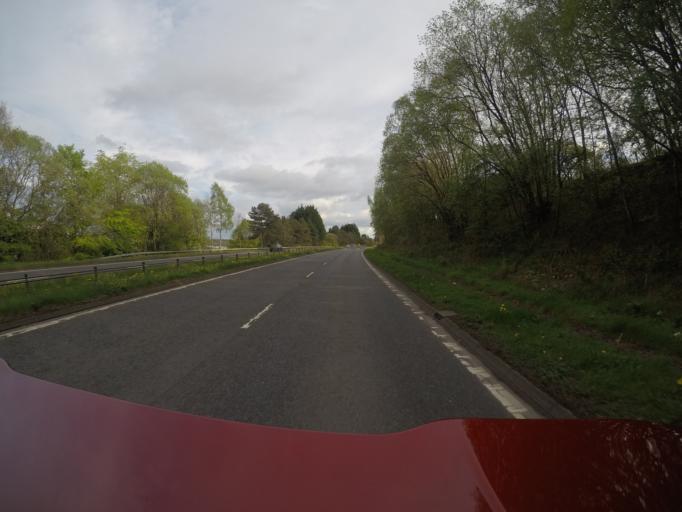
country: GB
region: Scotland
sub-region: West Dunbartonshire
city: Alexandria
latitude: 55.9874
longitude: -4.5888
